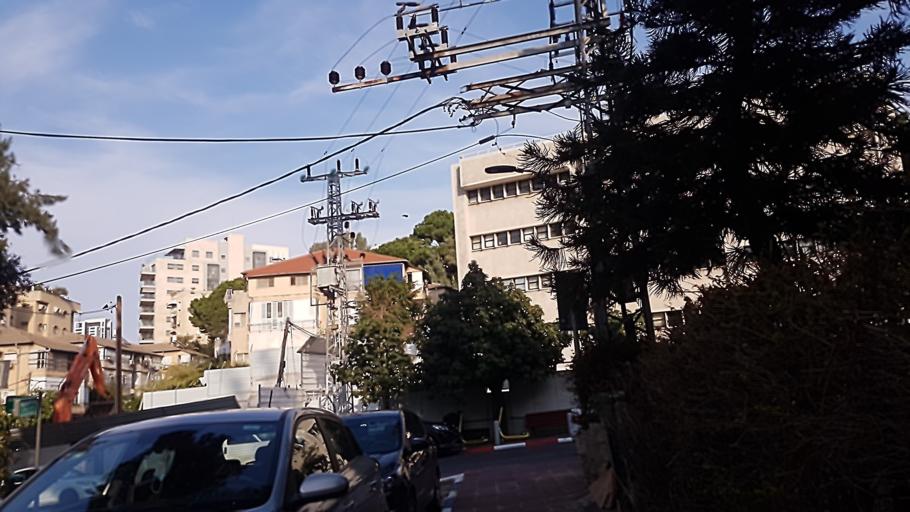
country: IL
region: Tel Aviv
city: Ramat Gan
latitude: 32.0827
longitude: 34.8095
